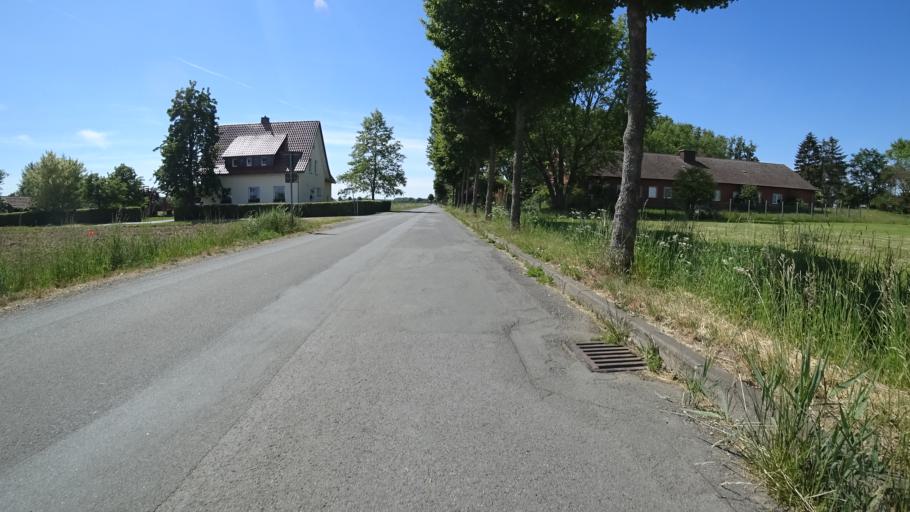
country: DE
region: North Rhine-Westphalia
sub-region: Regierungsbezirk Detmold
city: Rheda-Wiedenbruck
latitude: 51.8205
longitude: 8.2928
